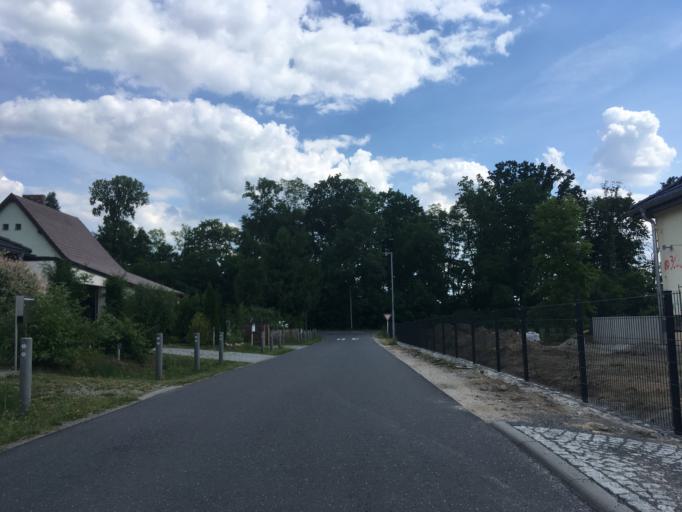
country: DE
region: Brandenburg
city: Muncheberg
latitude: 52.5014
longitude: 14.1101
